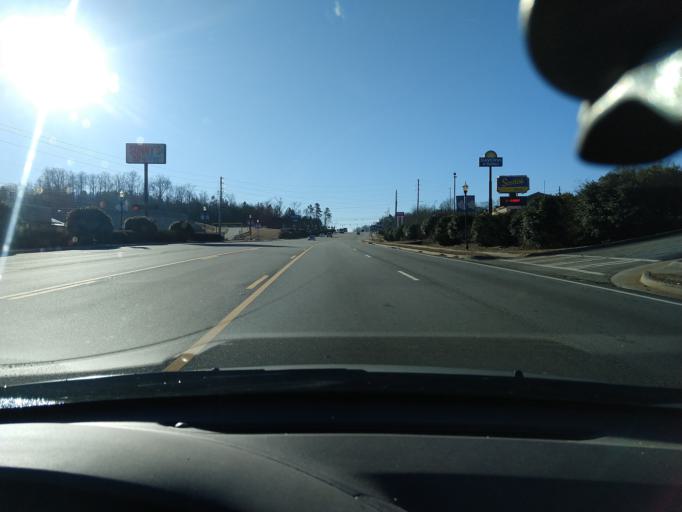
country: US
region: Georgia
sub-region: Jackson County
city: Commerce
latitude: 34.2486
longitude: -83.4600
